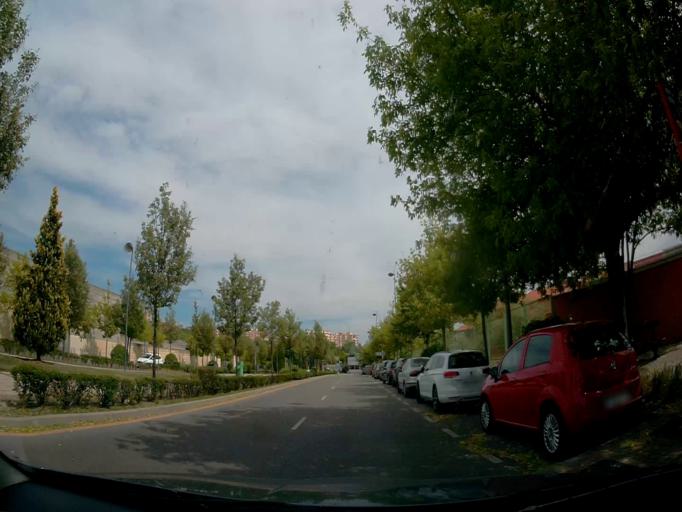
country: ES
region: Madrid
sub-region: Provincia de Madrid
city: Alcorcon
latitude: 40.3471
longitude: -3.8394
